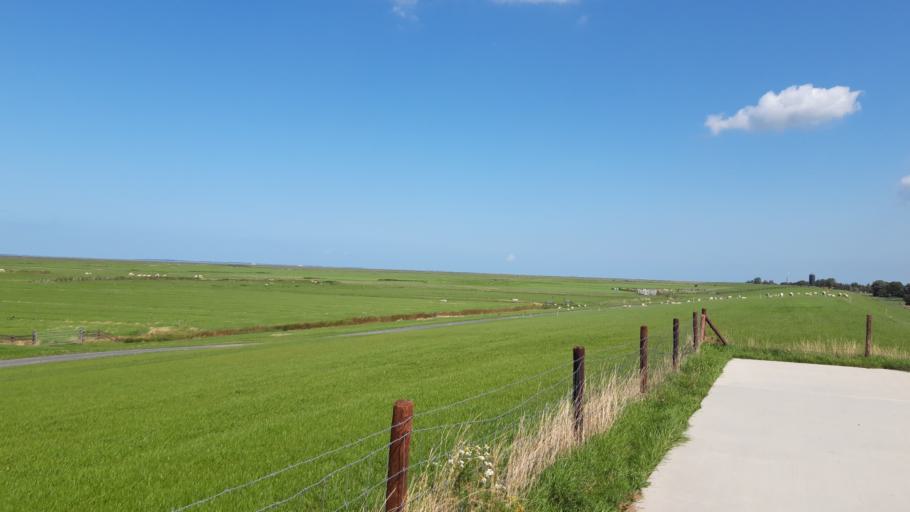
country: NL
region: Friesland
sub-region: Gemeente Ferwerderadiel
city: Hallum
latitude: 53.3215
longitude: 5.7590
